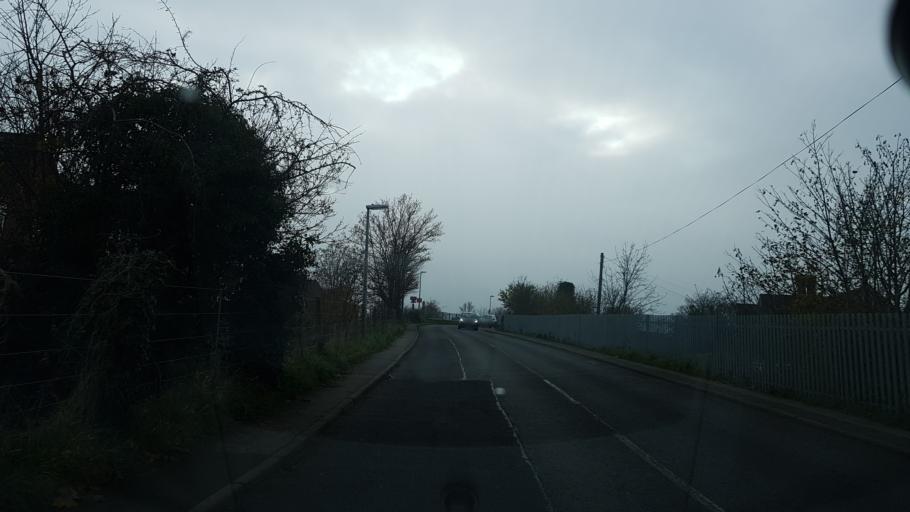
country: GB
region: England
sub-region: Central Bedfordshire
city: Biggleswade
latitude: 52.0919
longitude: -0.2601
